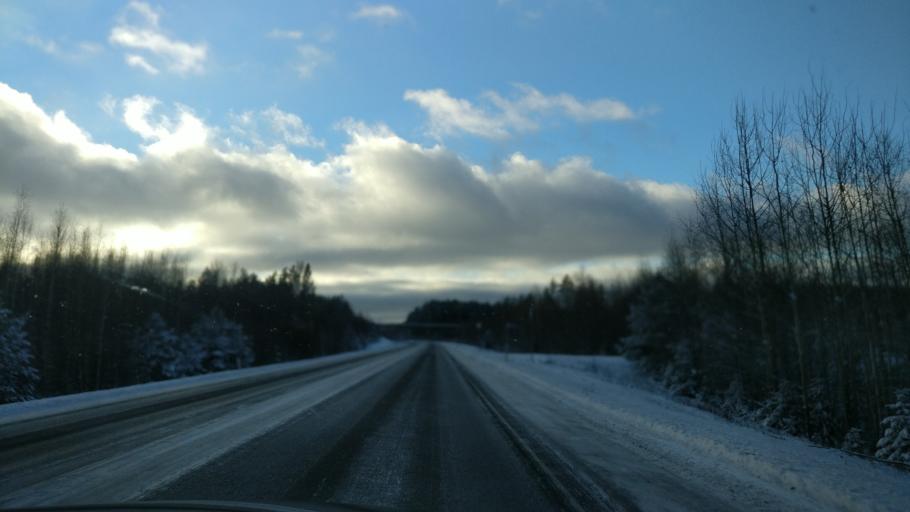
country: FI
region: Southern Savonia
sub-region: Mikkeli
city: Pertunmaa
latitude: 61.4294
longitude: 26.4640
